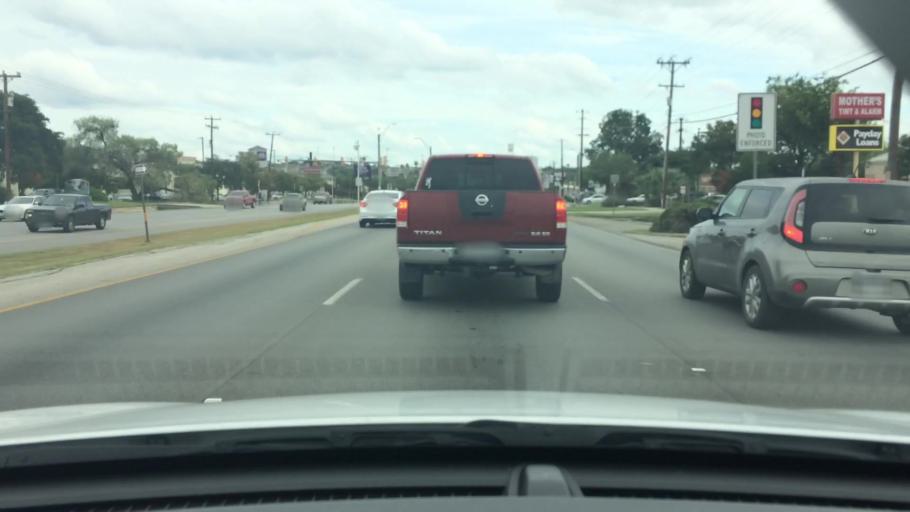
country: US
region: Texas
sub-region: Bexar County
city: Leon Valley
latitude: 29.4959
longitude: -98.6197
